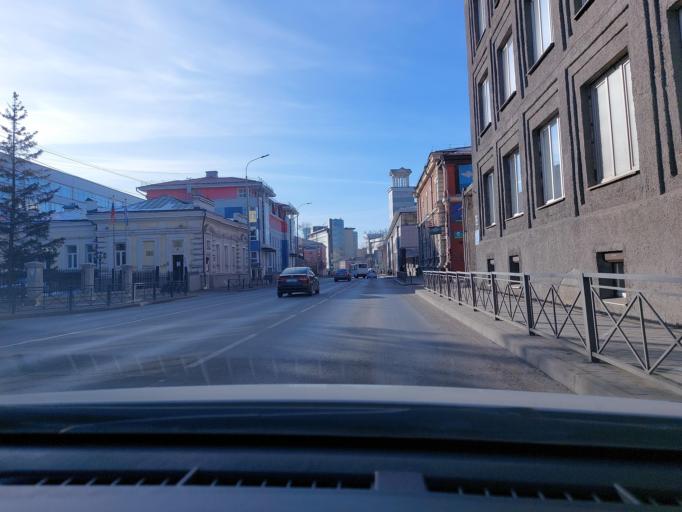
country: RU
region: Irkutsk
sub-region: Irkutskiy Rayon
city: Irkutsk
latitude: 52.2891
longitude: 104.2779
